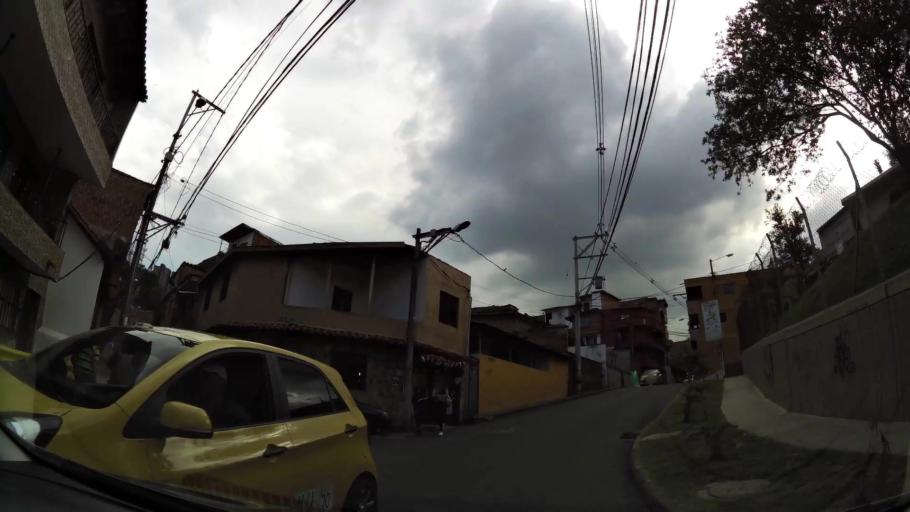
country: CO
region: Antioquia
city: Envigado
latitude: 6.1571
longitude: -75.5818
